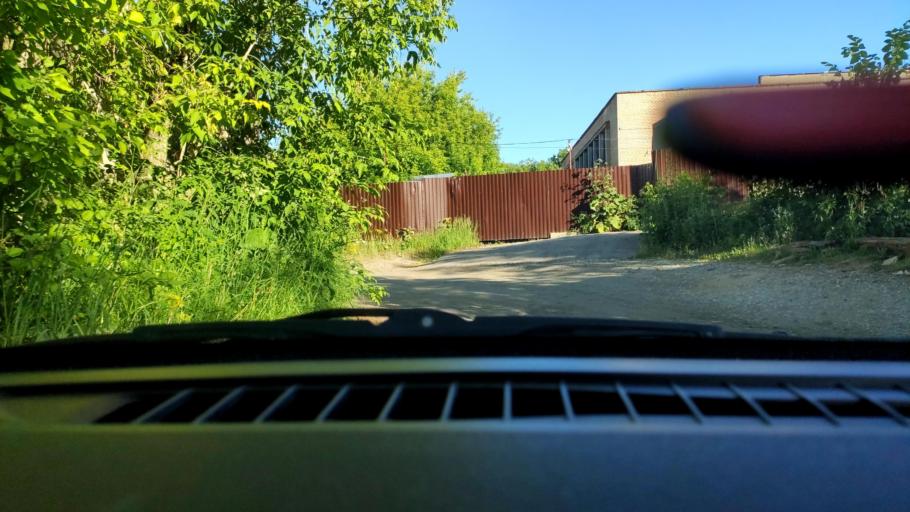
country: RU
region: Perm
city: Perm
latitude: 57.9754
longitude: 56.2172
